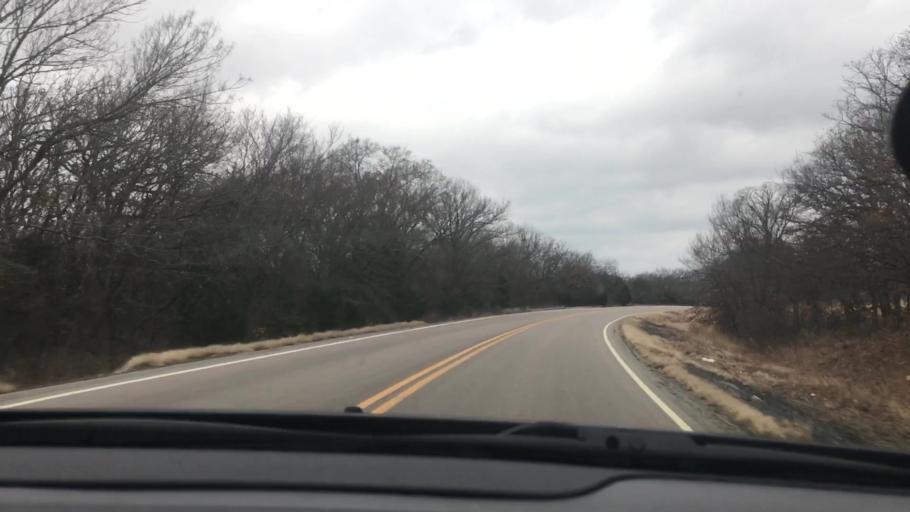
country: US
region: Oklahoma
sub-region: Coal County
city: Coalgate
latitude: 34.3695
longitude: -96.3813
